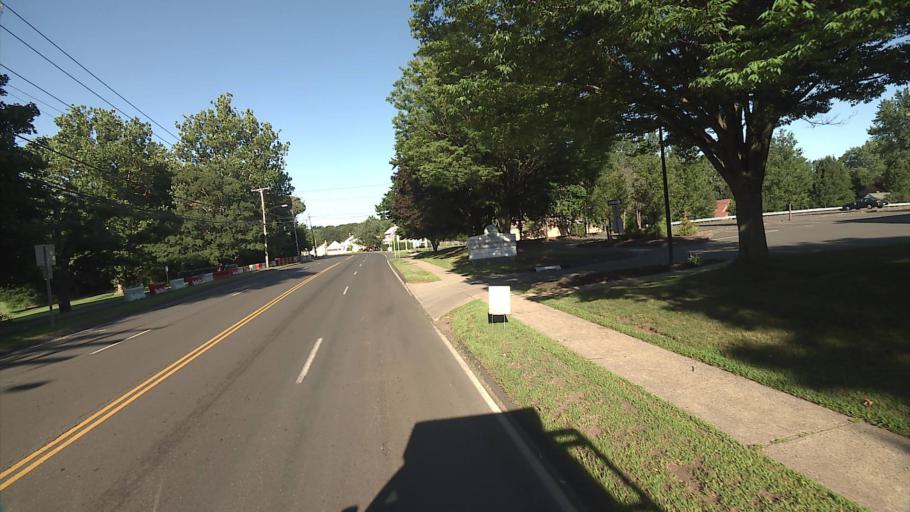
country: US
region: Connecticut
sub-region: New Haven County
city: Hamden
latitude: 41.3828
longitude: -72.9086
